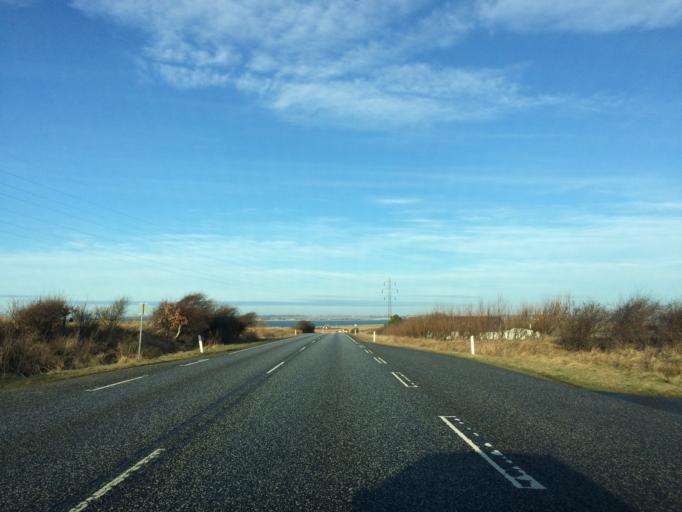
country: DK
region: Central Jutland
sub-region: Struer Kommune
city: Struer
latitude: 56.5550
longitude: 8.5579
